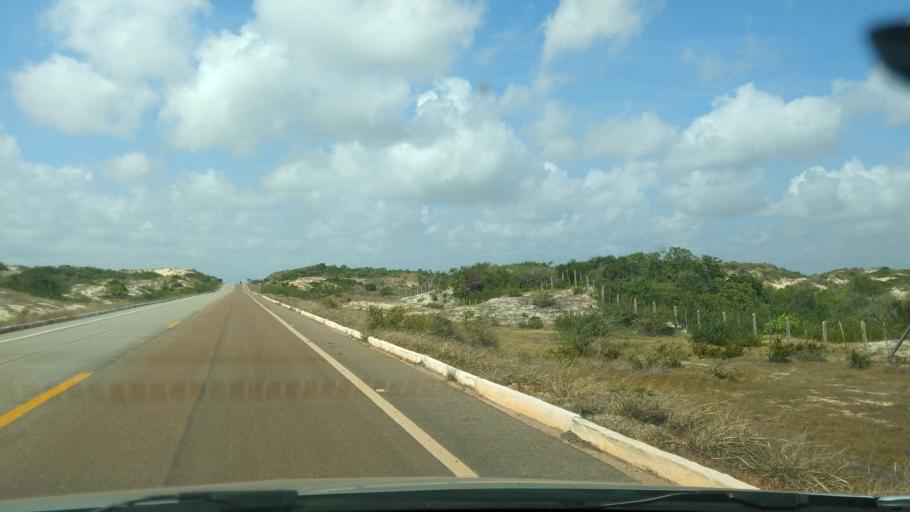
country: BR
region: Rio Grande do Norte
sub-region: Touros
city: Touros
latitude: -5.1597
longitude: -35.5010
